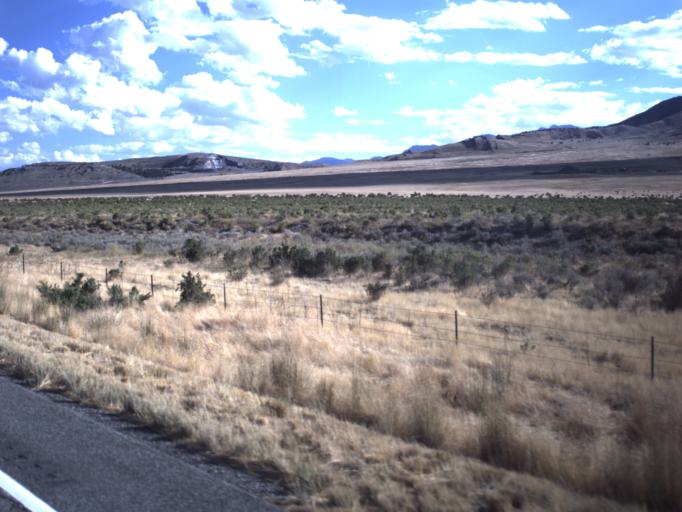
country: US
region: Utah
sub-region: Tooele County
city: Grantsville
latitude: 40.6662
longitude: -112.5435
